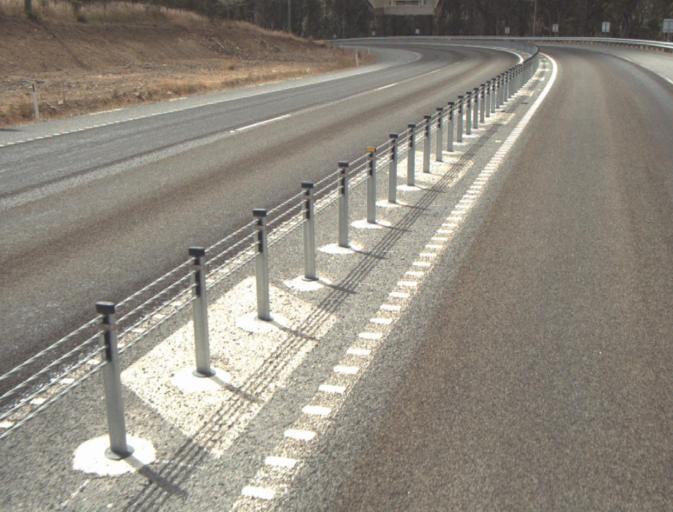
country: AU
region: Tasmania
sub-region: Launceston
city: Mayfield
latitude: -41.2983
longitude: 147.0495
